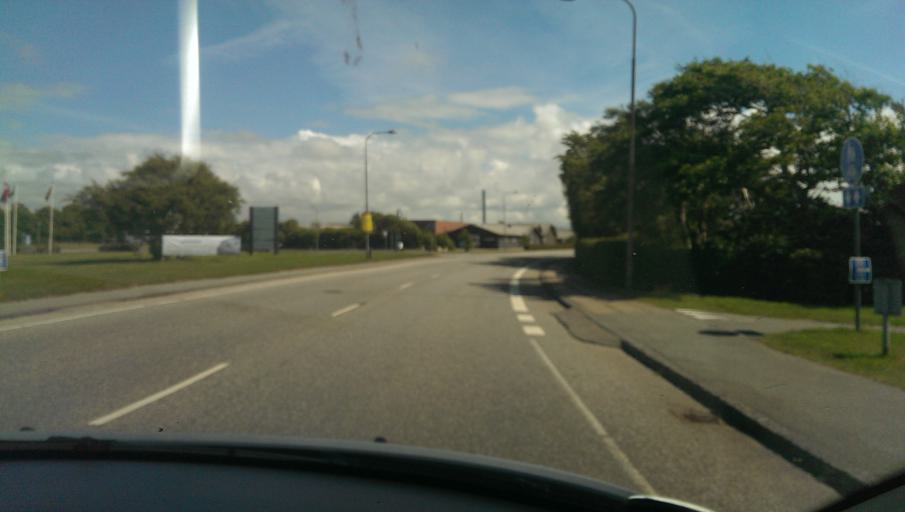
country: DK
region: Central Jutland
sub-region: Ringkobing-Skjern Kommune
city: Ringkobing
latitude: 56.0952
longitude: 8.2343
